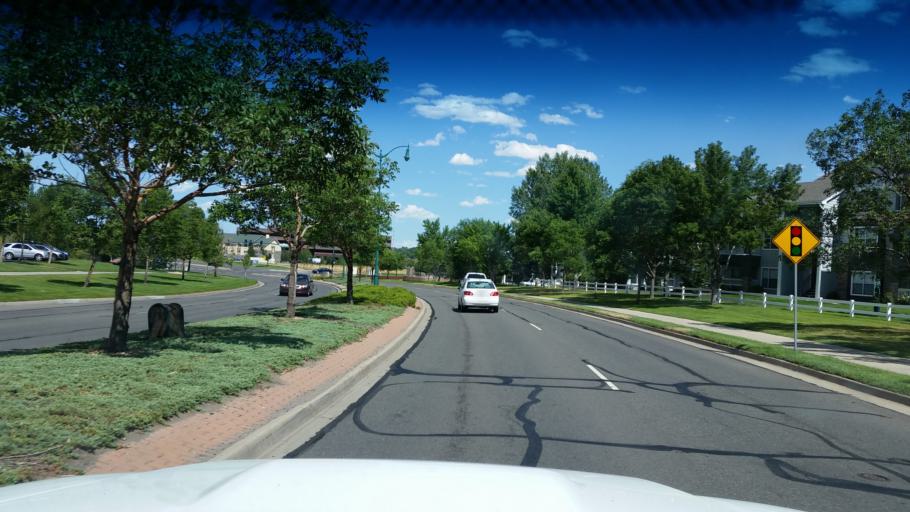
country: US
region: Colorado
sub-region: Broomfield County
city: Broomfield
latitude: 39.8799
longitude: -105.0795
